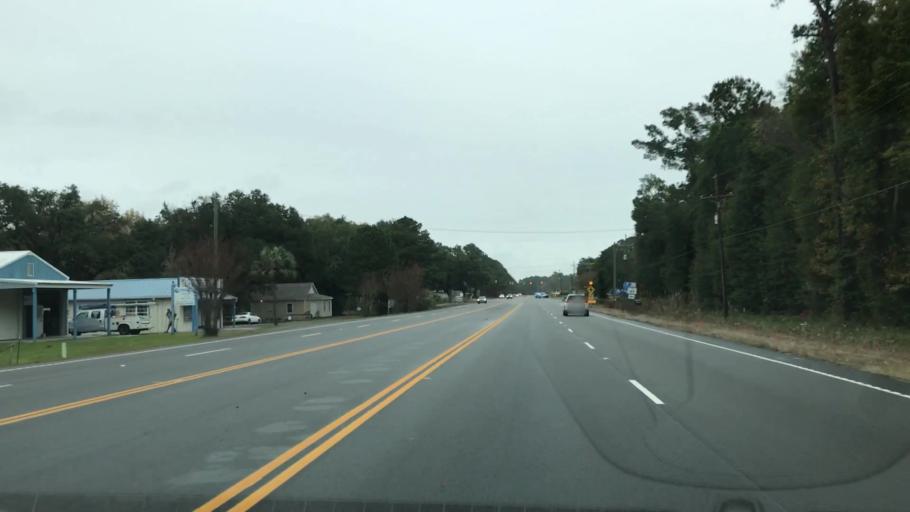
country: US
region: South Carolina
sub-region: Charleston County
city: Awendaw
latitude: 33.0938
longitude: -79.4785
